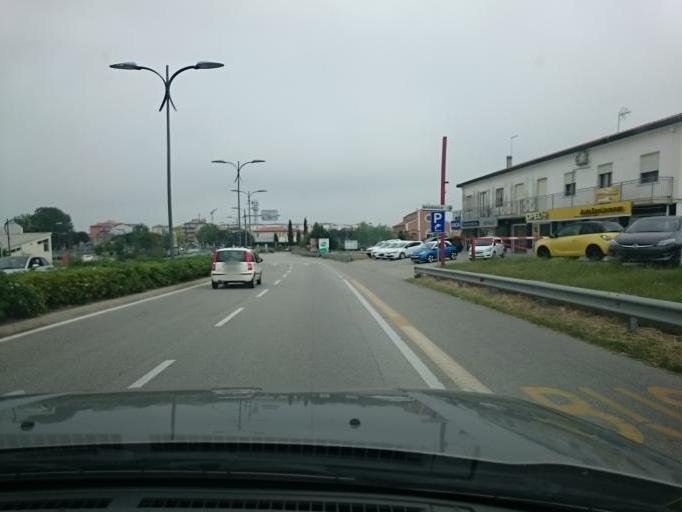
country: IT
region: Veneto
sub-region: Provincia di Venezia
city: Chioggia
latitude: 45.1968
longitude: 12.2806
